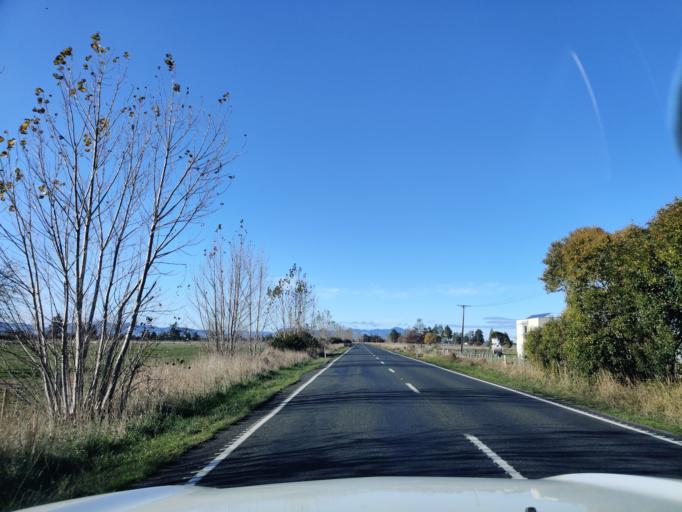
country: NZ
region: Waikato
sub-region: Hauraki District
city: Ngatea
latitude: -37.3022
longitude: 175.5593
